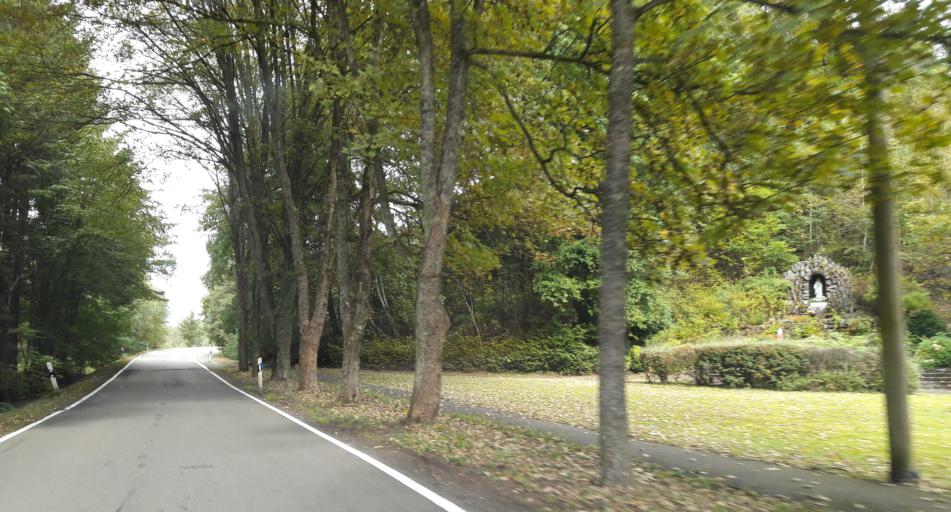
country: DE
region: Rheinland-Pfalz
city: Hahnweiler
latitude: 49.5195
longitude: 7.2112
